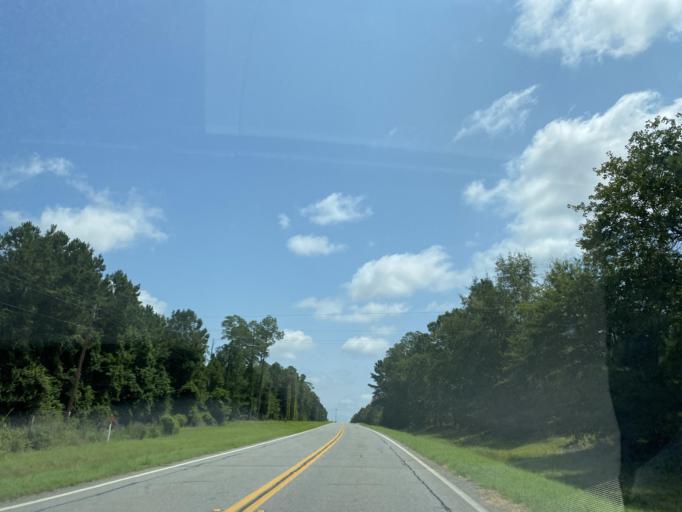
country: US
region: Georgia
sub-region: Wilcox County
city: Abbeville
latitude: 31.9921
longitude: -83.1927
